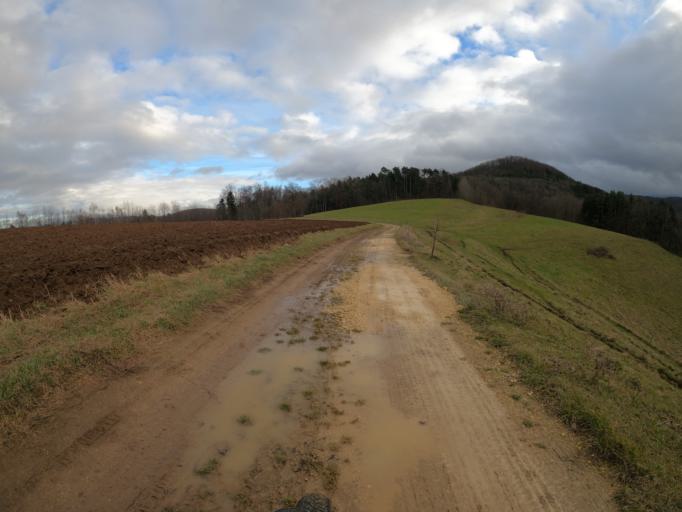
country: DE
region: Baden-Wuerttemberg
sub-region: Regierungsbezirk Stuttgart
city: Waldstetten
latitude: 48.7581
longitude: 9.8447
